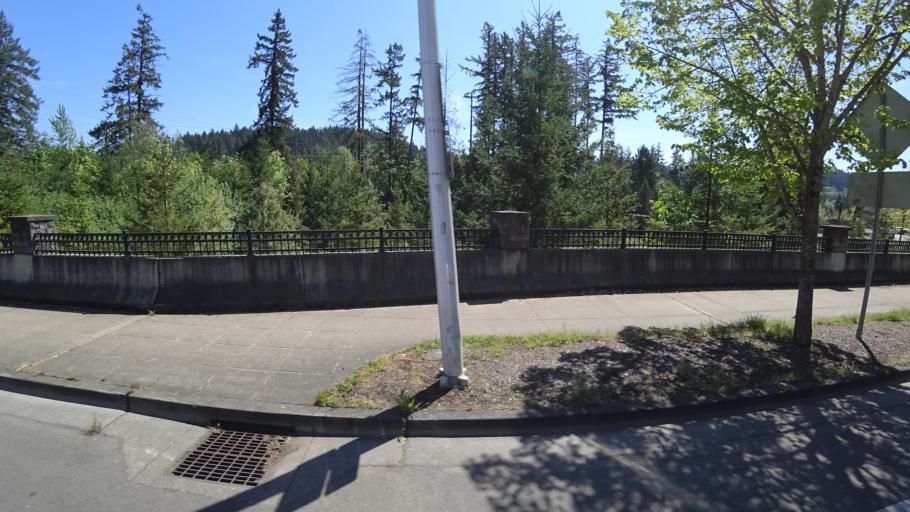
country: US
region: Oregon
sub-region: Washington County
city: King City
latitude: 45.4304
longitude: -122.8276
